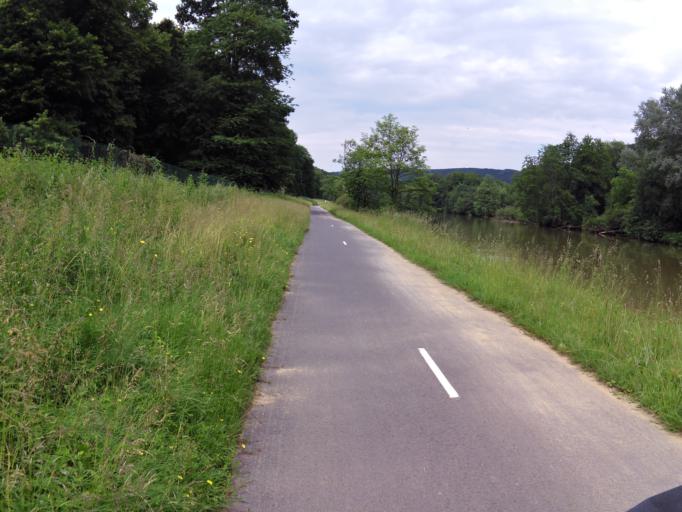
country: FR
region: Champagne-Ardenne
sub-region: Departement des Ardennes
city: Nouzonville
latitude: 49.8026
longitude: 4.7512
